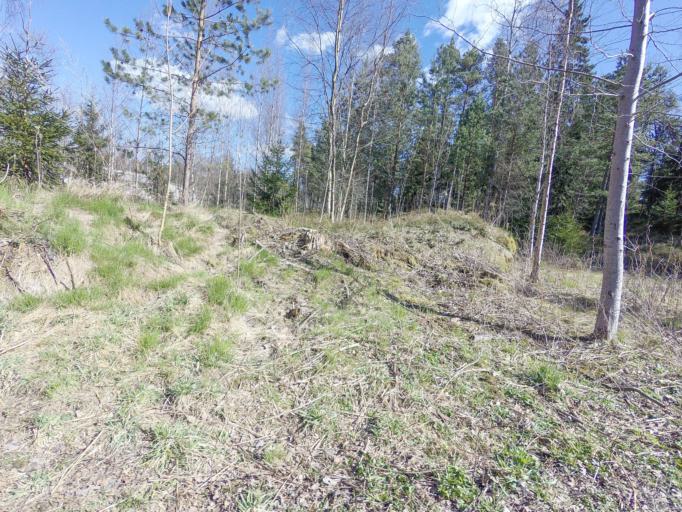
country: FI
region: Uusimaa
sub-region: Helsinki
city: Helsinki
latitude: 60.1599
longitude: 25.0694
